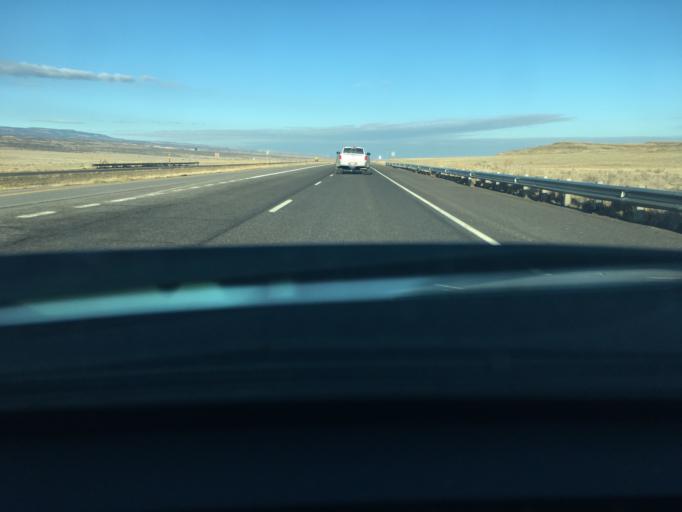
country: US
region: Colorado
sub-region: Mesa County
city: Palisade
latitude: 38.8710
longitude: -108.3368
